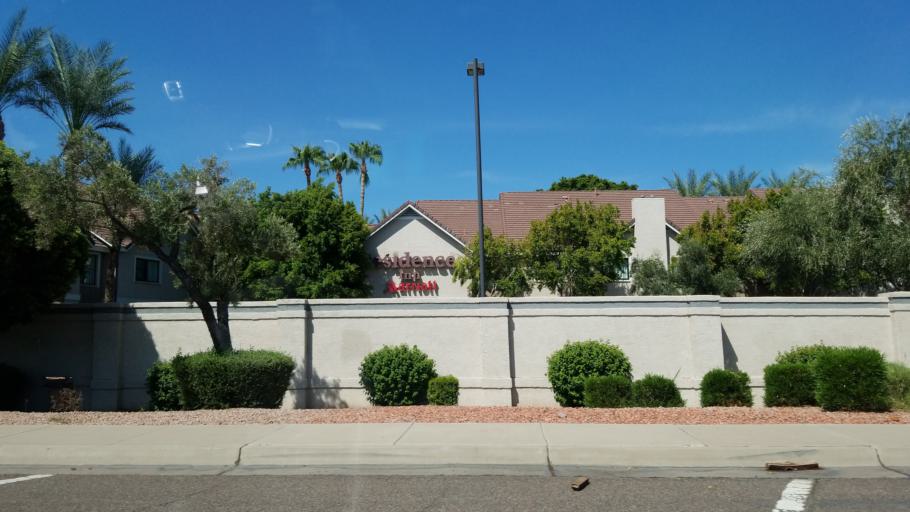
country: US
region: Arizona
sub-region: Maricopa County
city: Glendale
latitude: 33.5573
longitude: -112.1134
